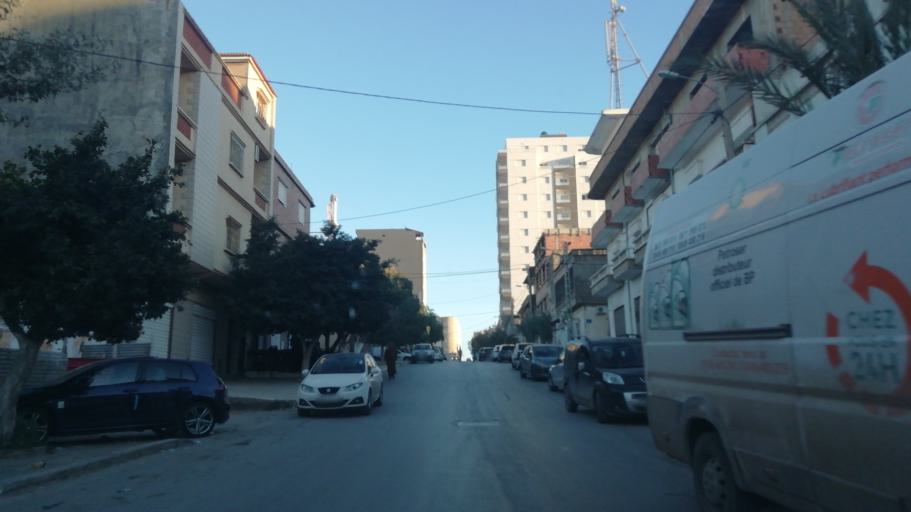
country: DZ
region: Oran
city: Bir el Djir
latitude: 35.7283
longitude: -0.5790
